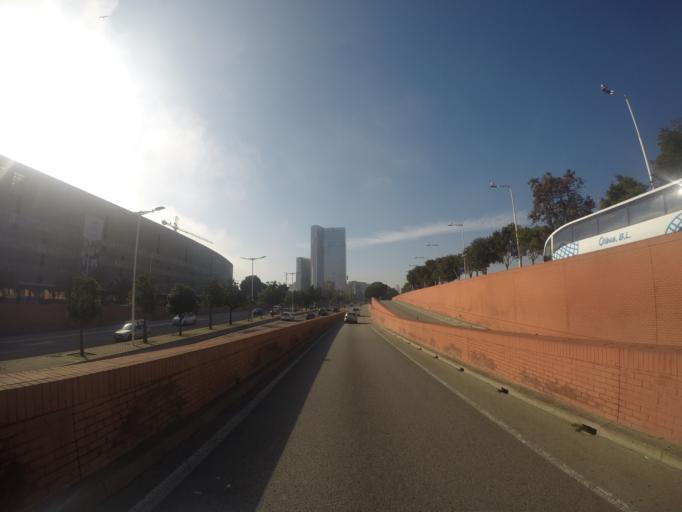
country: ES
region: Catalonia
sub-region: Provincia de Barcelona
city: Ciutat Vella
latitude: 41.3858
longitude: 2.1933
